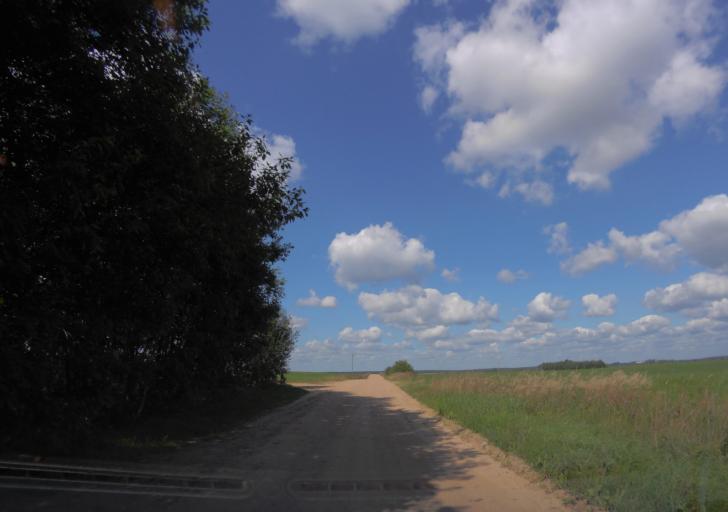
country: BY
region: Minsk
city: Horad Barysaw
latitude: 54.3646
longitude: 28.4648
